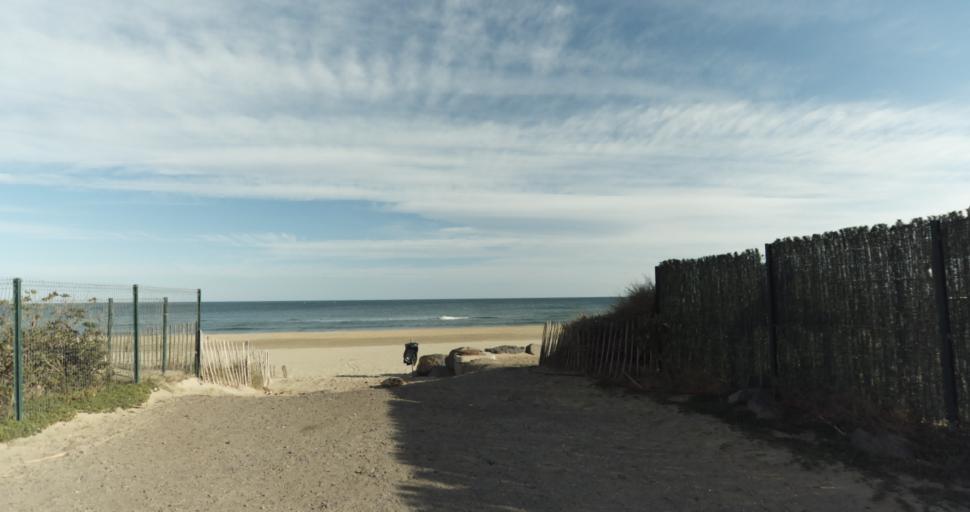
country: FR
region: Languedoc-Roussillon
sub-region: Departement de l'Herault
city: Le Cap d'Agde
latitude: 43.3071
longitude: 3.5438
